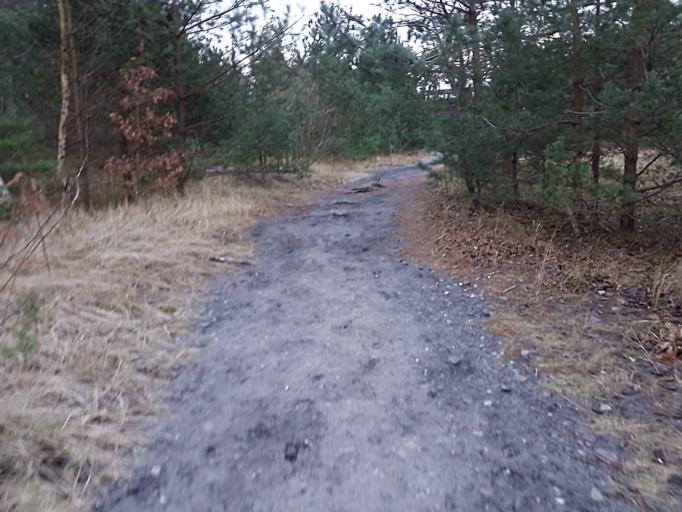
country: DE
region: Mecklenburg-Vorpommern
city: Ostseebad Binz
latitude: 54.4405
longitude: 13.5751
